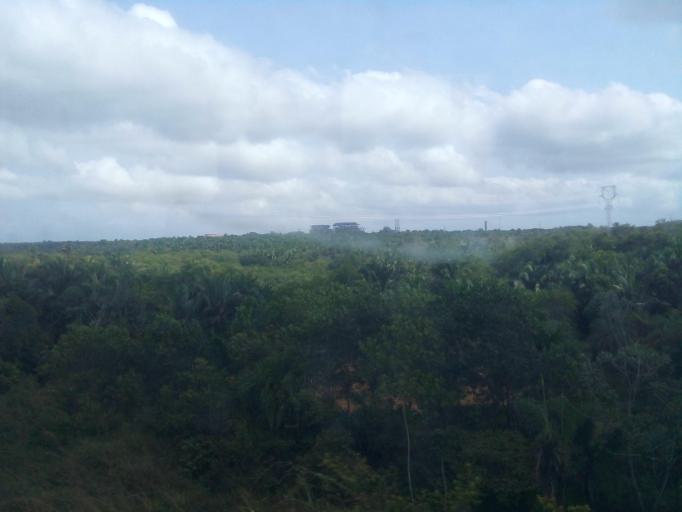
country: BR
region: Maranhao
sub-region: Sao Luis
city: Sao Luis
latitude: -2.7335
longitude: -44.3445
